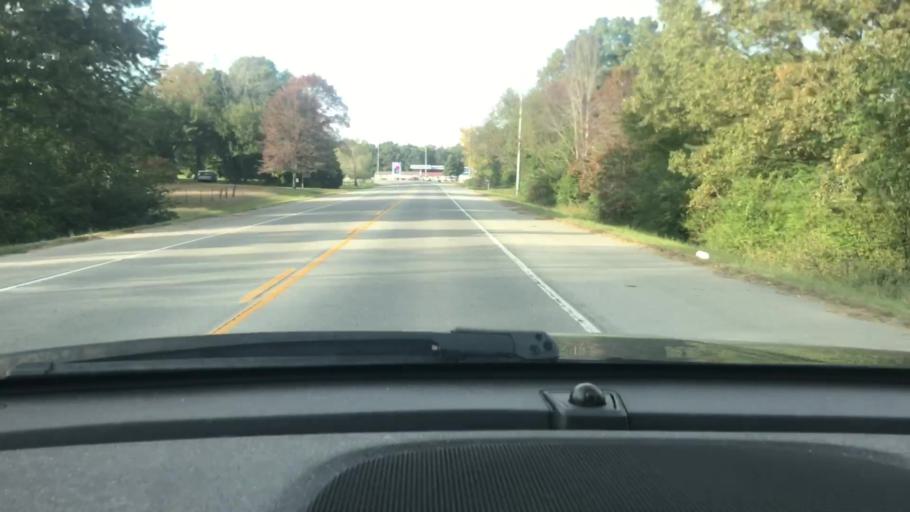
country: US
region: Tennessee
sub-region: Dickson County
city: White Bluff
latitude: 36.1234
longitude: -87.2270
